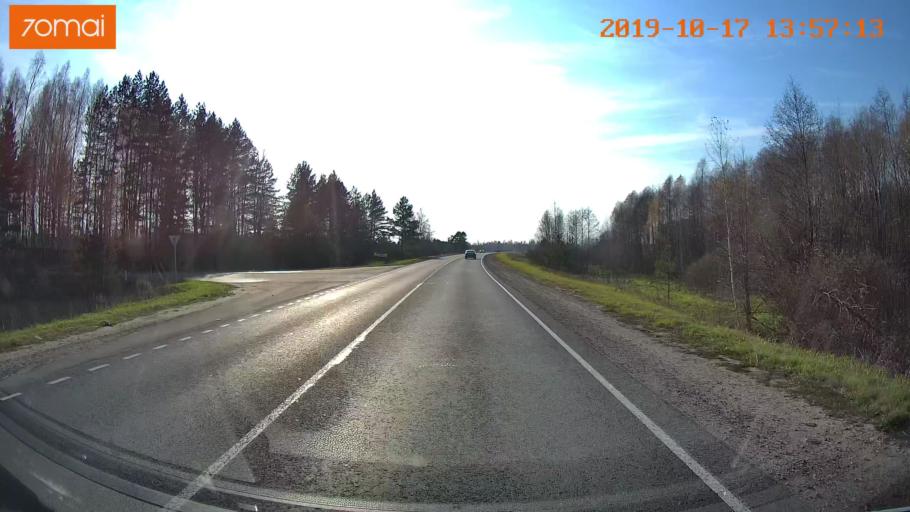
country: RU
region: Rjazan
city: Spas-Klepiki
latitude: 55.1454
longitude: 40.2508
